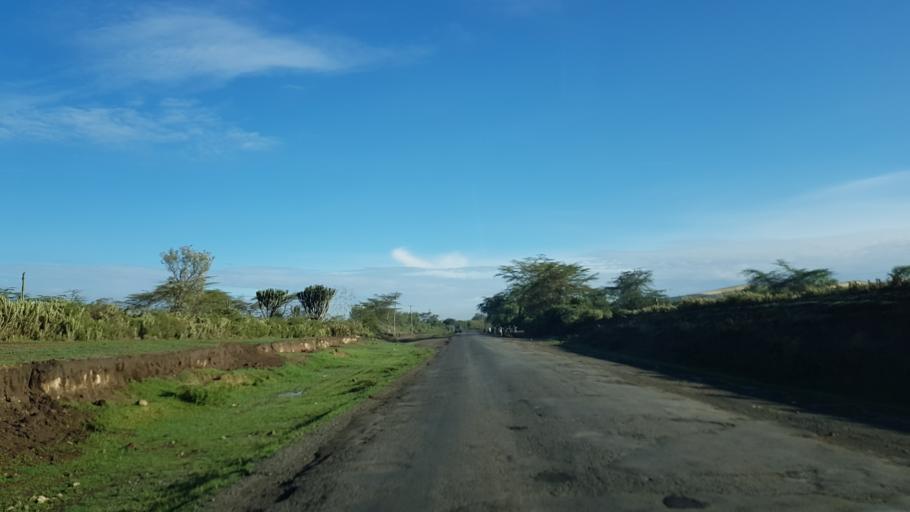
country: KE
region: Nakuru
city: Naivasha
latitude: -0.7854
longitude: 36.4256
